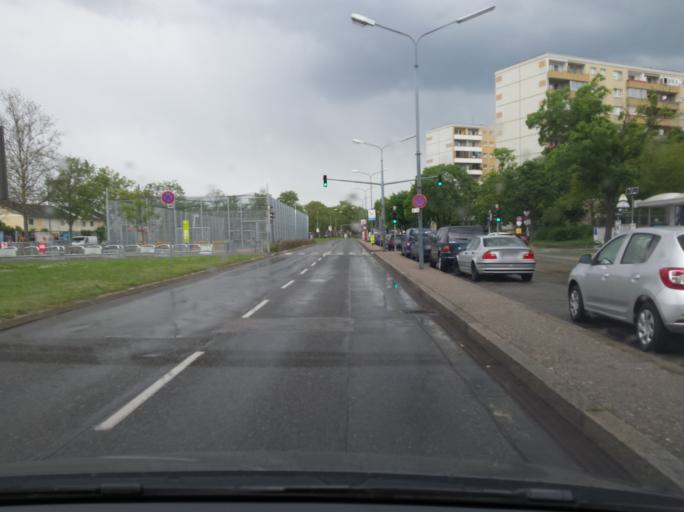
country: AT
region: Lower Austria
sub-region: Politischer Bezirk Wien-Umgebung
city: Gerasdorf bei Wien
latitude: 48.2382
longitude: 16.4398
